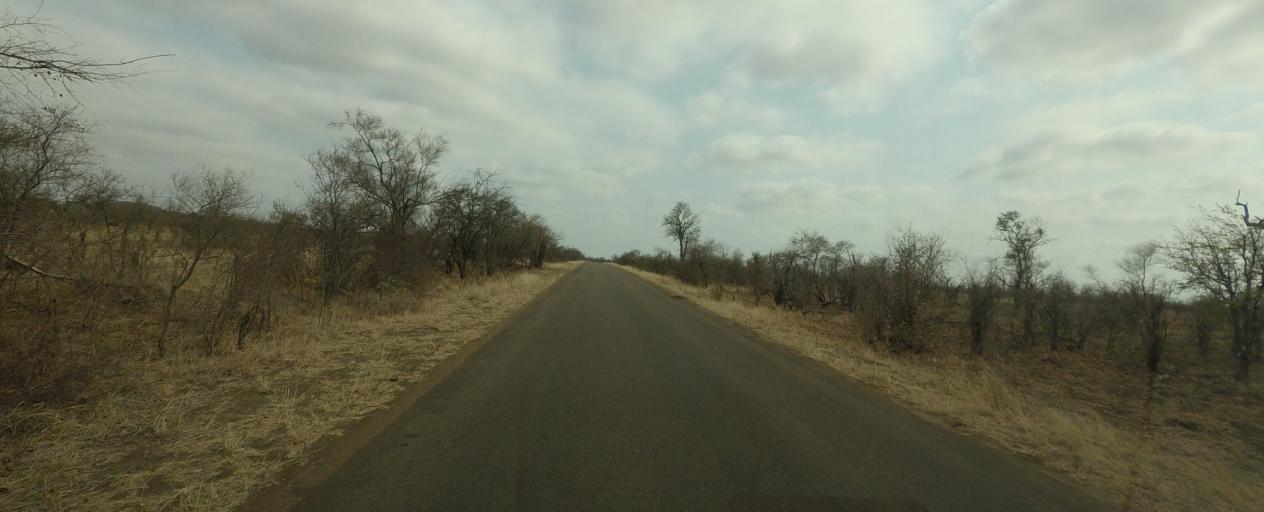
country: ZA
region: Limpopo
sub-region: Vhembe District Municipality
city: Mutale
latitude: -22.6207
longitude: 31.1760
